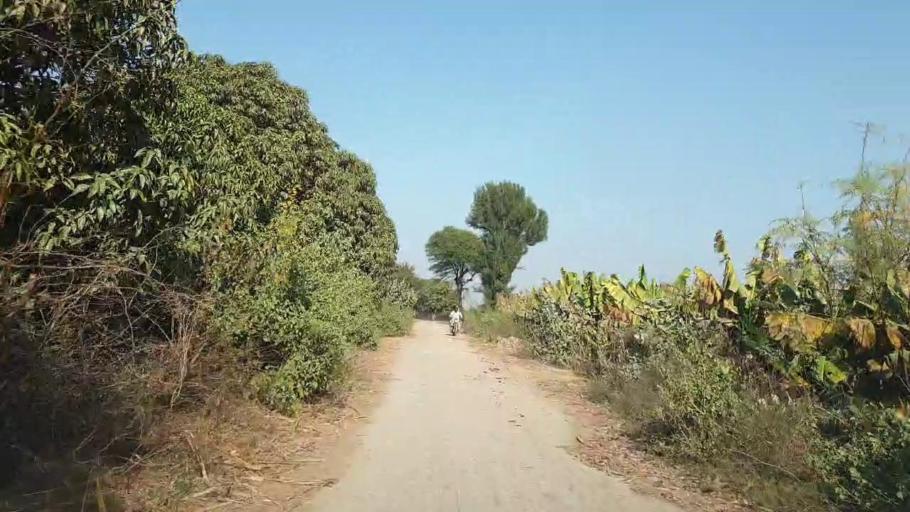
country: PK
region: Sindh
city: Tando Jam
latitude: 25.5061
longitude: 68.5377
